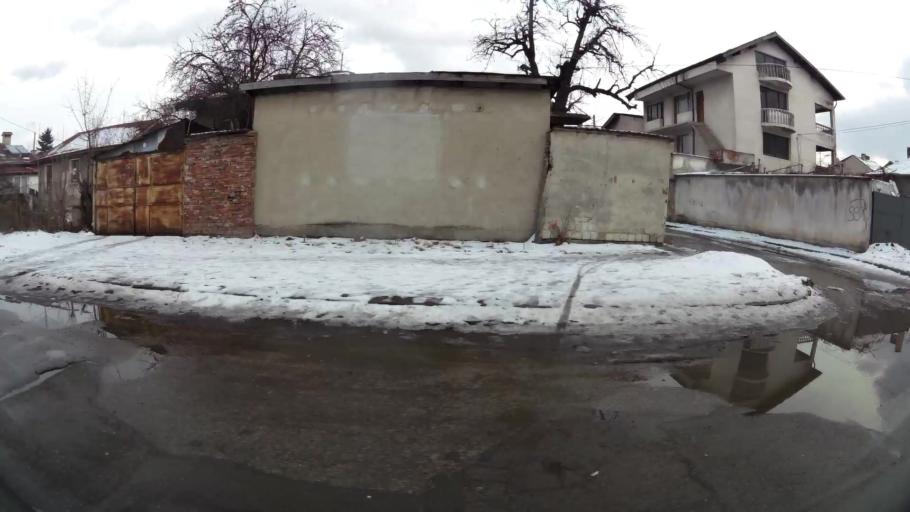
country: BG
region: Sofia-Capital
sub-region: Stolichna Obshtina
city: Sofia
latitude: 42.6879
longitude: 23.3825
